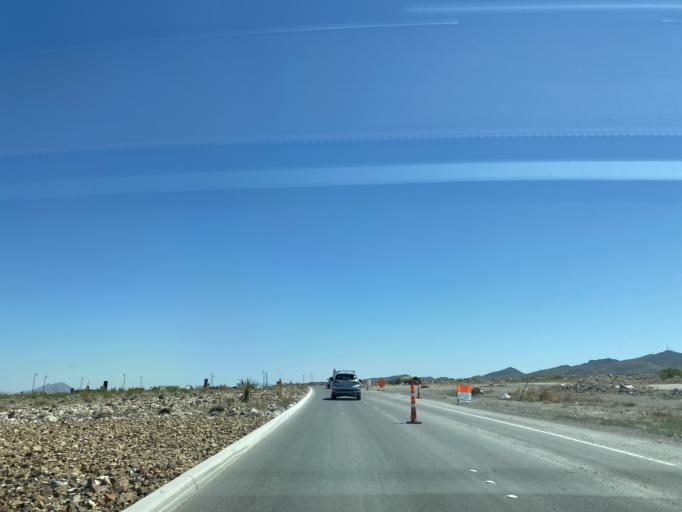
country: US
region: Nevada
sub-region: Clark County
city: Enterprise
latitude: 35.9378
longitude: -115.1356
